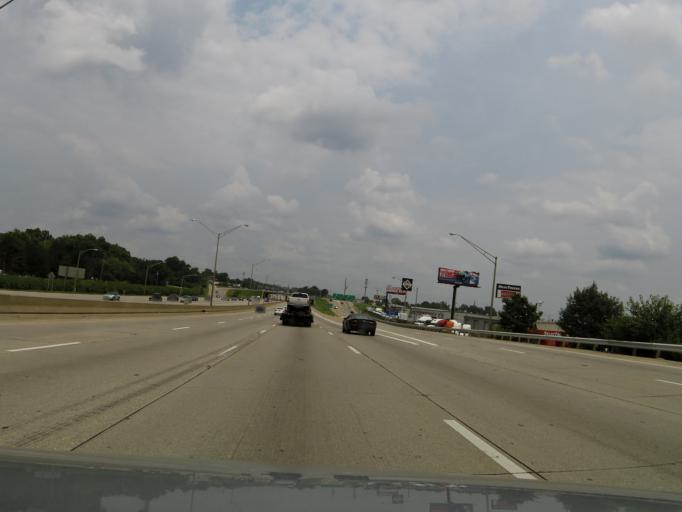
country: US
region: Kentucky
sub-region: Jefferson County
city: Audubon Park
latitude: 38.1926
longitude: -85.7124
